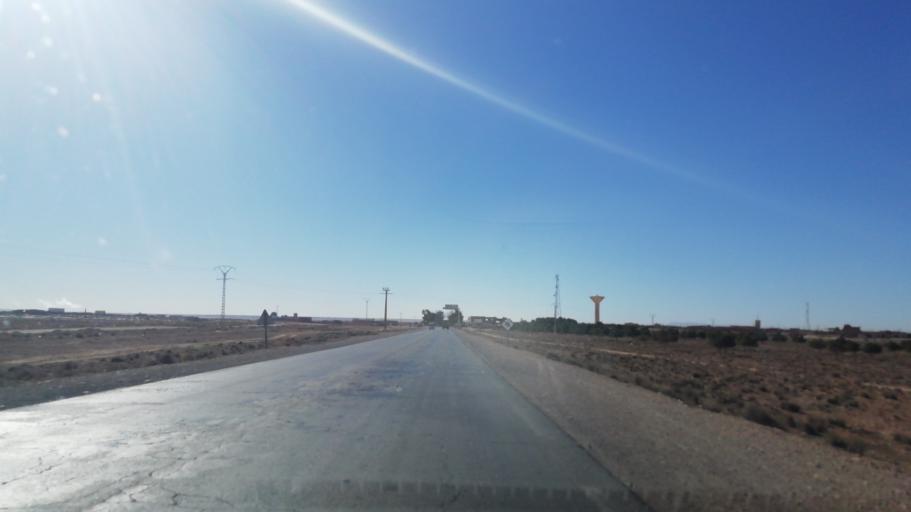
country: DZ
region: Saida
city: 'Ain el Hadjar
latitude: 34.1618
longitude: 0.0717
